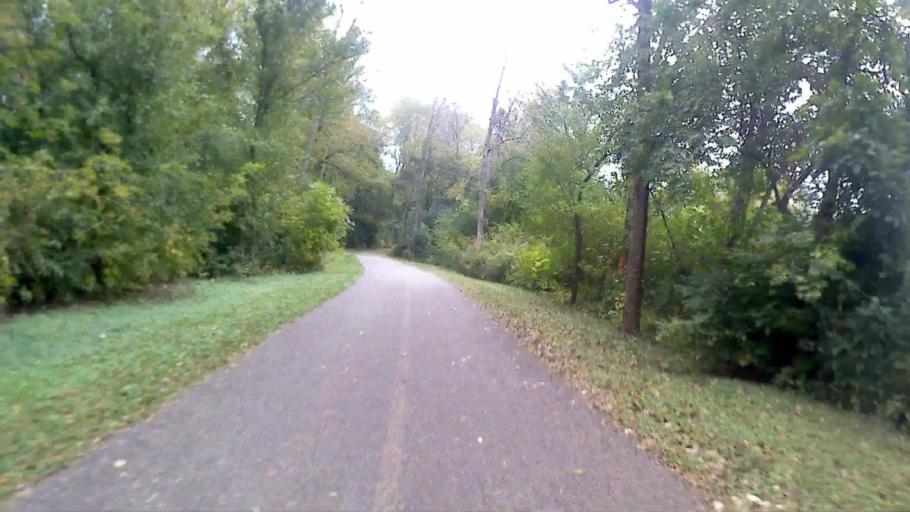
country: US
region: Illinois
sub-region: Kane County
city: Montgomery
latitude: 41.7457
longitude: -88.3568
